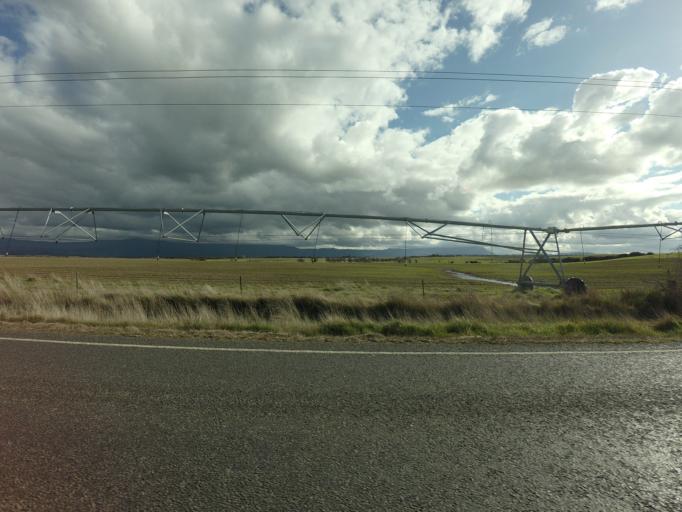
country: AU
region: Tasmania
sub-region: Northern Midlands
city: Longford
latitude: -41.7053
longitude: 147.0784
